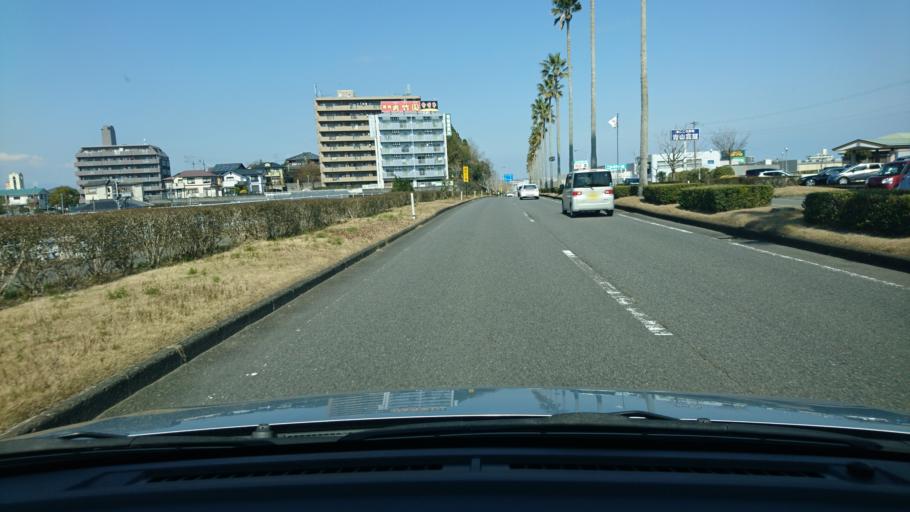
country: JP
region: Miyazaki
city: Miyazaki-shi
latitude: 31.8827
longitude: 131.4109
